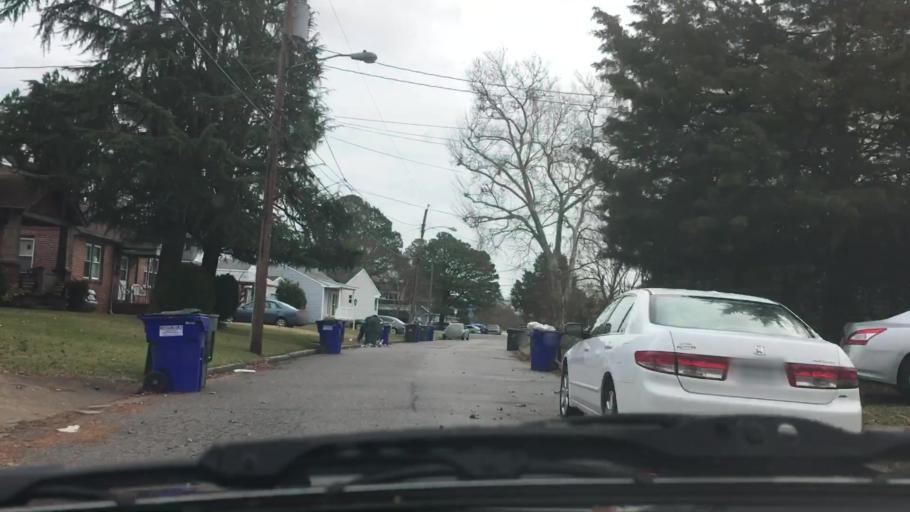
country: US
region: Virginia
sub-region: City of Norfolk
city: Norfolk
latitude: 36.8807
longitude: -76.2491
